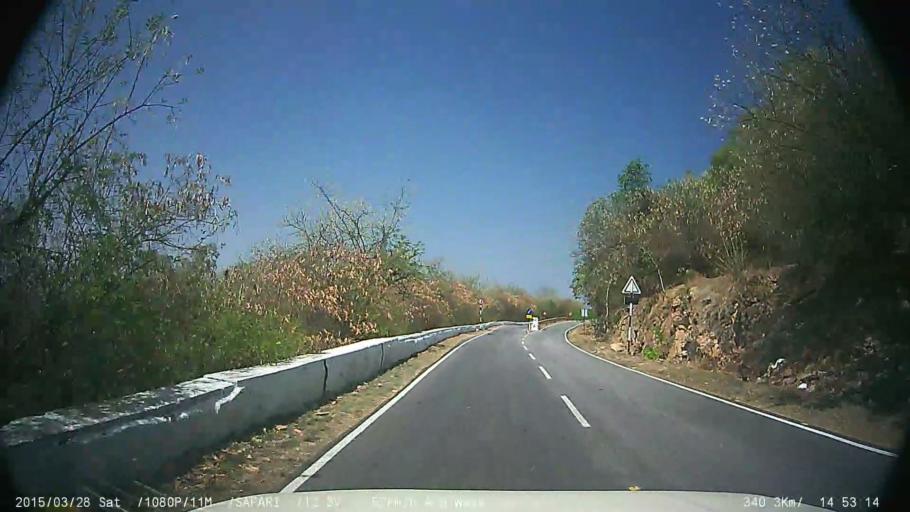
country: IN
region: Karnataka
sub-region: Mysore
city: Mysore
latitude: 12.2851
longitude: 76.6958
